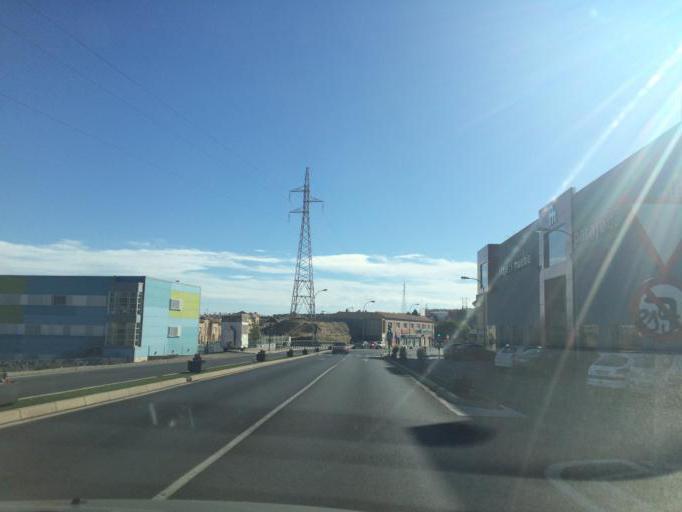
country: ES
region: Andalusia
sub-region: Provincia de Almeria
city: Huercal de Almeria
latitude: 36.8714
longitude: -2.4402
